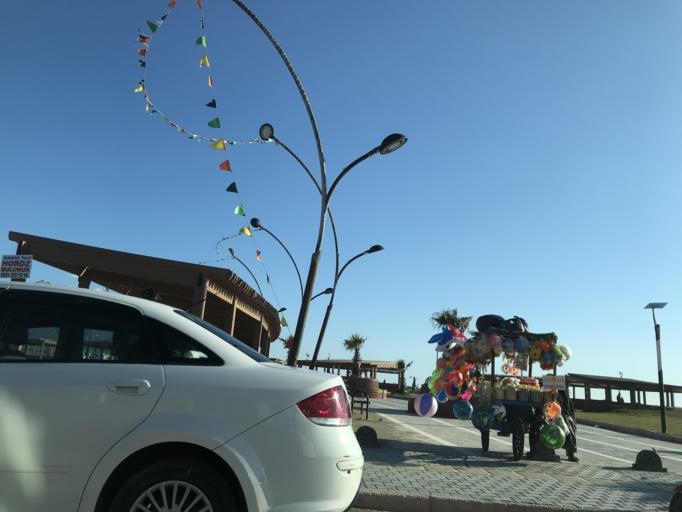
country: TR
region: Hatay
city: Samandag
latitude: 36.0816
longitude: 35.9462
